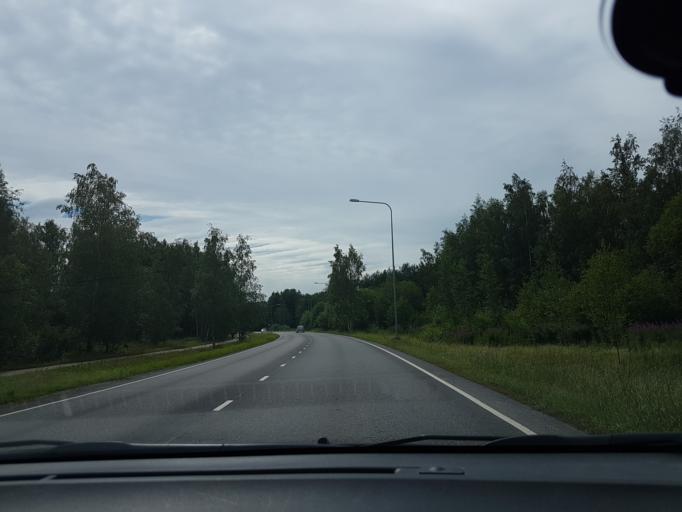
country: FI
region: Uusimaa
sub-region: Helsinki
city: Vantaa
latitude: 60.2605
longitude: 25.0390
